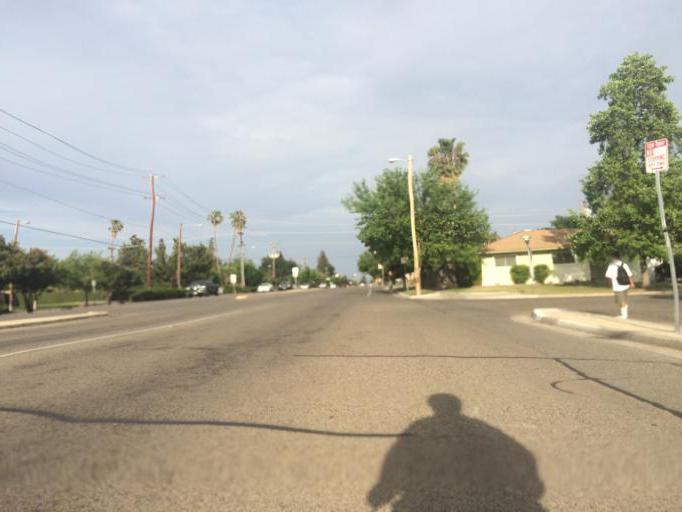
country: US
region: California
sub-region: Fresno County
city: Clovis
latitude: 36.8157
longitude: -119.7668
